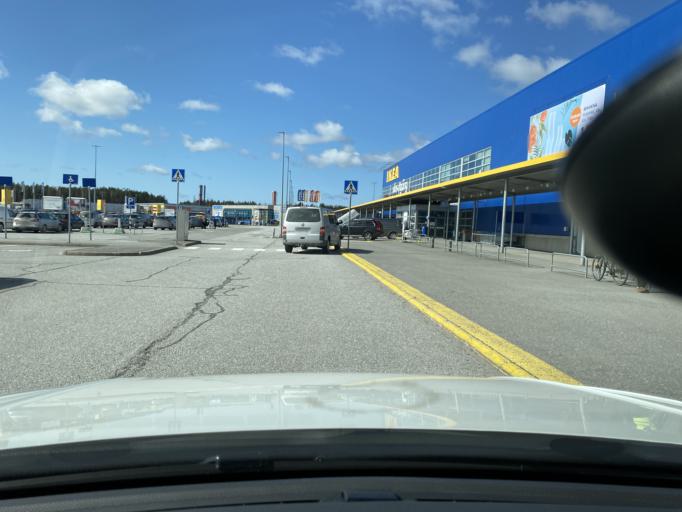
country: FI
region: Varsinais-Suomi
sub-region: Turku
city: Rusko
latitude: 60.4943
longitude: 22.2291
